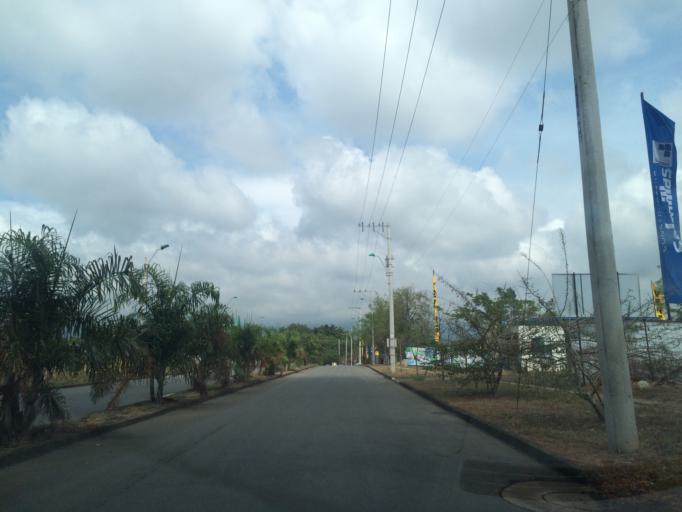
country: CO
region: Valle del Cauca
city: Cali
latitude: 3.3564
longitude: -76.5215
